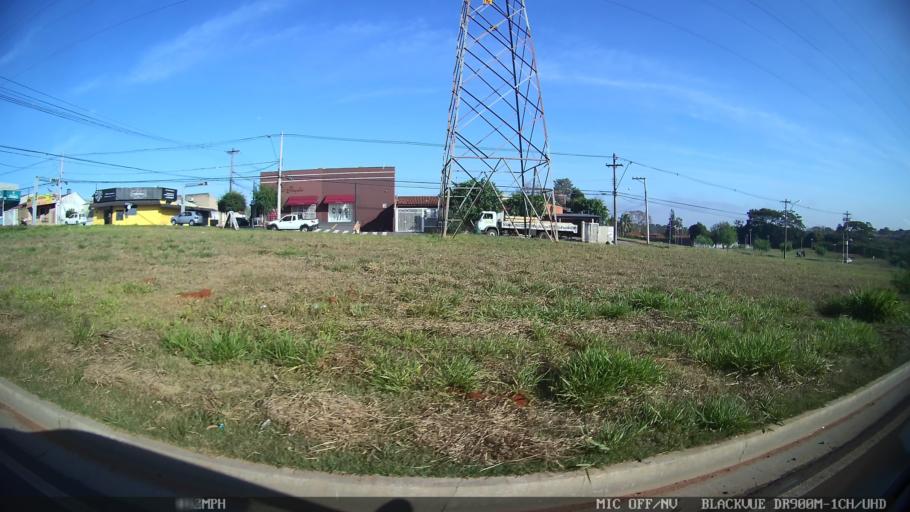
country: BR
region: Sao Paulo
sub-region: Sao Jose Do Rio Preto
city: Sao Jose do Rio Preto
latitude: -20.7868
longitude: -49.3436
